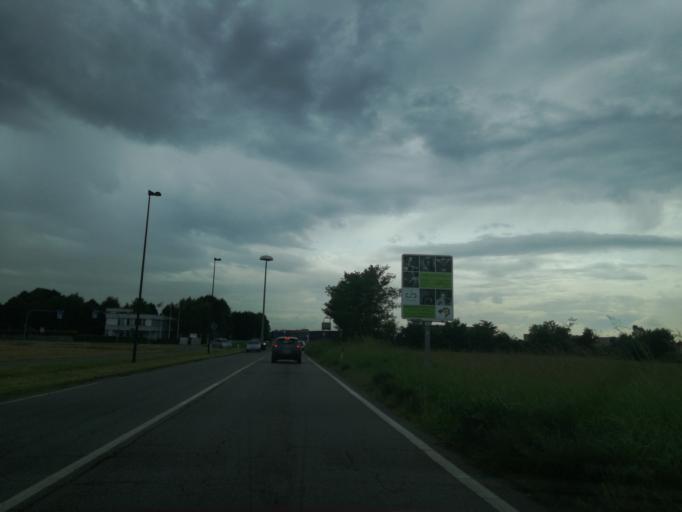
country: IT
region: Lombardy
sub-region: Provincia di Monza e Brianza
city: Ornago
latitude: 45.6086
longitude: 9.4193
